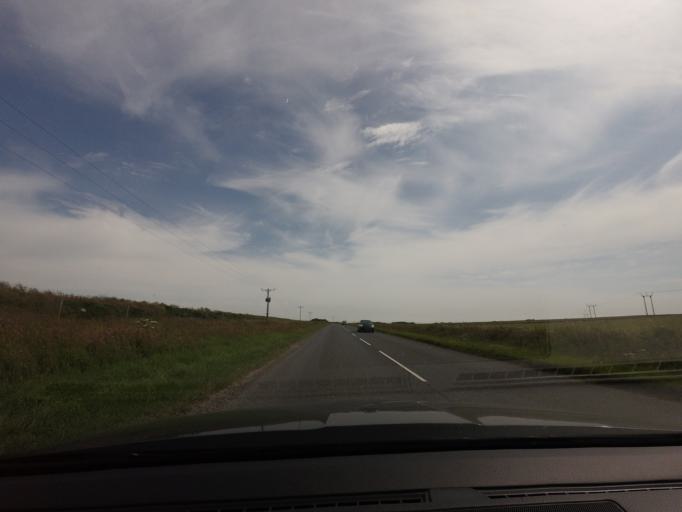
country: GB
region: Scotland
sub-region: Aberdeenshire
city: Peterhead
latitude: 57.5087
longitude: -1.8767
